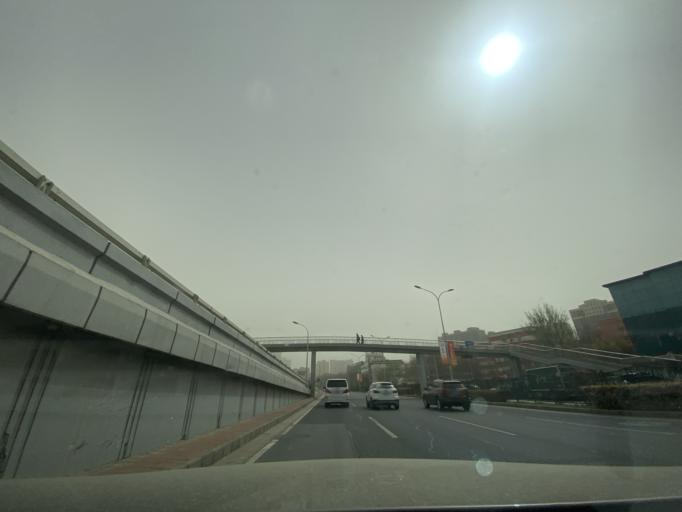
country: CN
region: Beijing
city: Sijiqing
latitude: 39.9394
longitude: 116.3080
